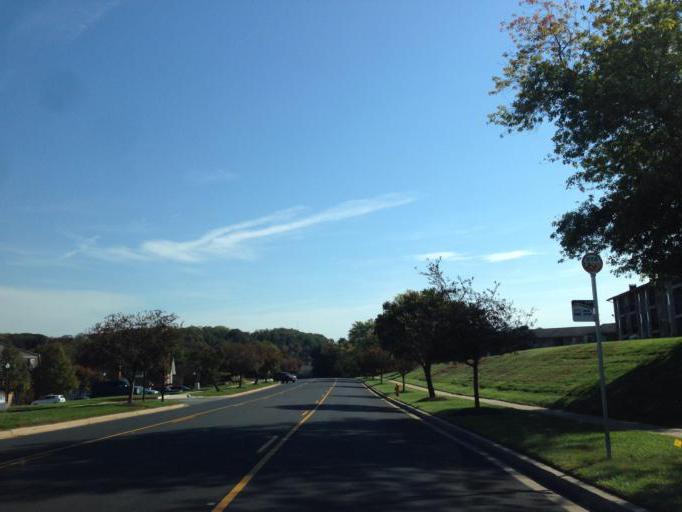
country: US
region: Maryland
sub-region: Howard County
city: Ellicott City
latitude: 39.2871
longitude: -76.8160
